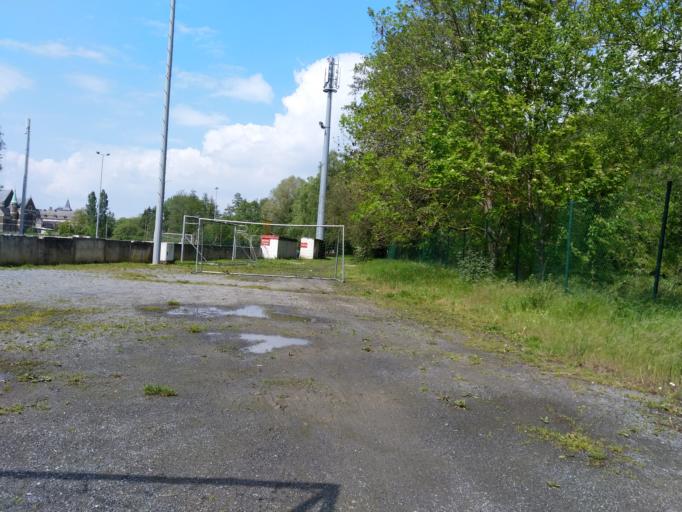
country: BE
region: Wallonia
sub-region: Province du Hainaut
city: Chasse Royale
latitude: 50.4382
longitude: 3.9661
